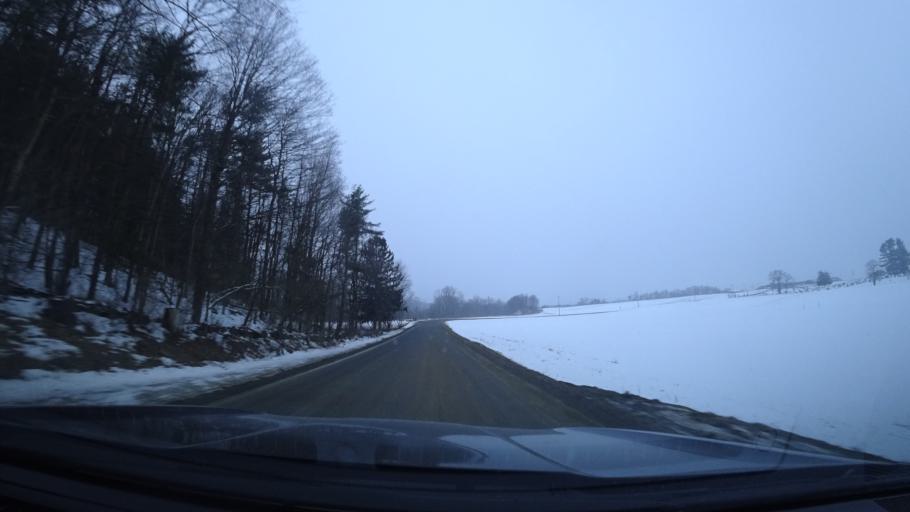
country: US
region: New York
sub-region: Washington County
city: Cambridge
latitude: 43.1600
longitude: -73.3472
